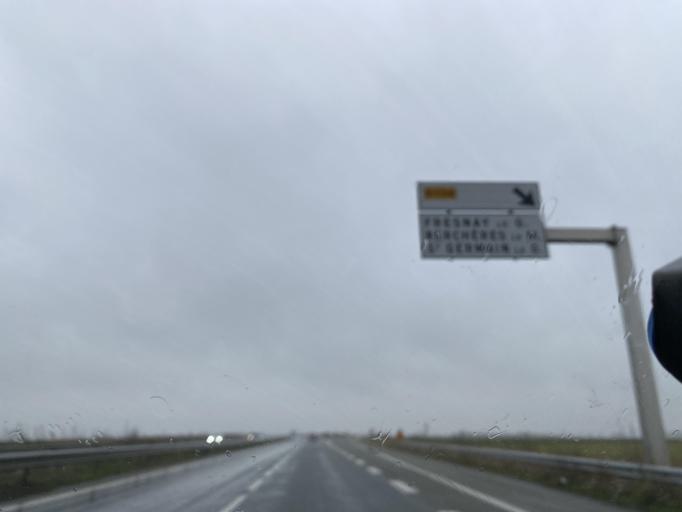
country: FR
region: Centre
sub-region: Departement d'Eure-et-Loir
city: Bailleau-l'Eveque
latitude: 48.5432
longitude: 1.4494
